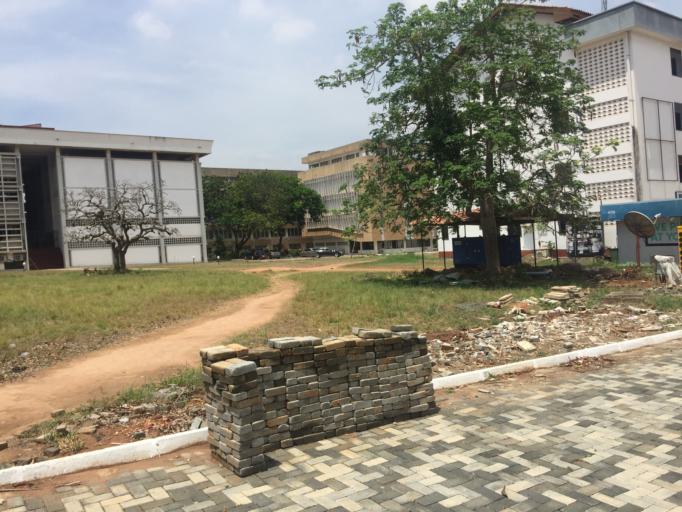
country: GH
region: Greater Accra
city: Medina Estates
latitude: 5.6520
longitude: -0.1886
